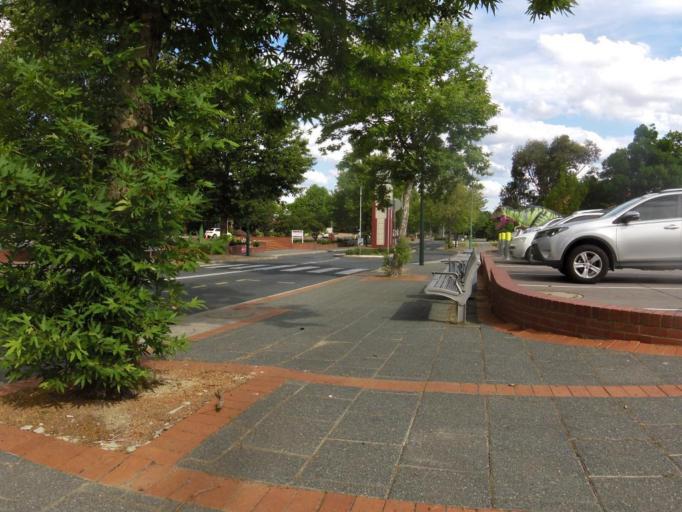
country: AU
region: Australian Capital Territory
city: Belconnen
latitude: -35.1904
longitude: 149.0833
